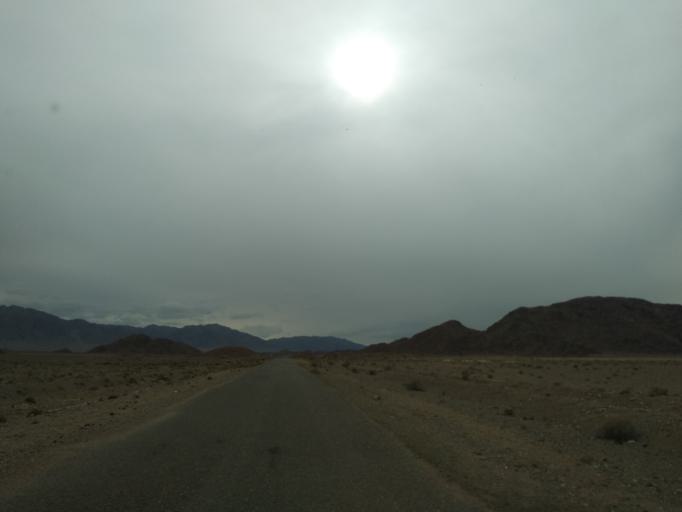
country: KG
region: Ysyk-Koel
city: Balykchy
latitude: 42.3156
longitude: 76.1547
